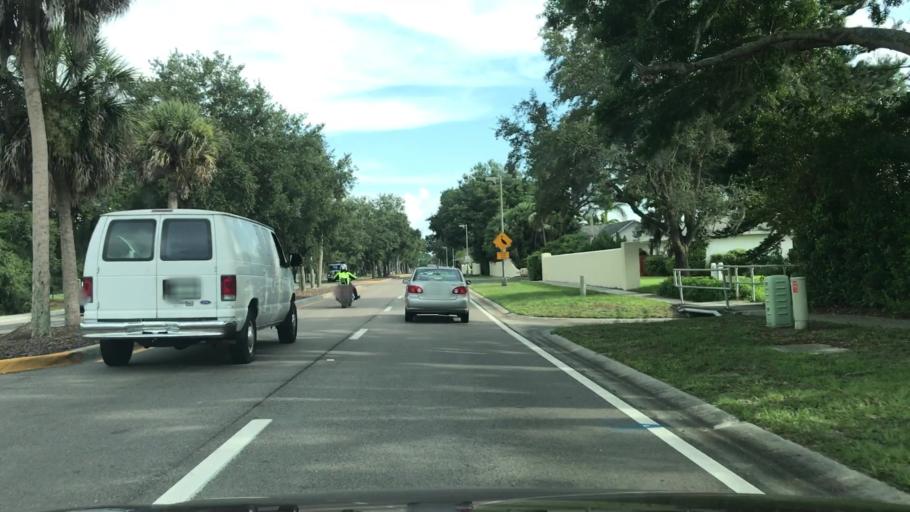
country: US
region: Florida
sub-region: Sarasota County
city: Plantation
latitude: 27.0763
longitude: -82.3890
